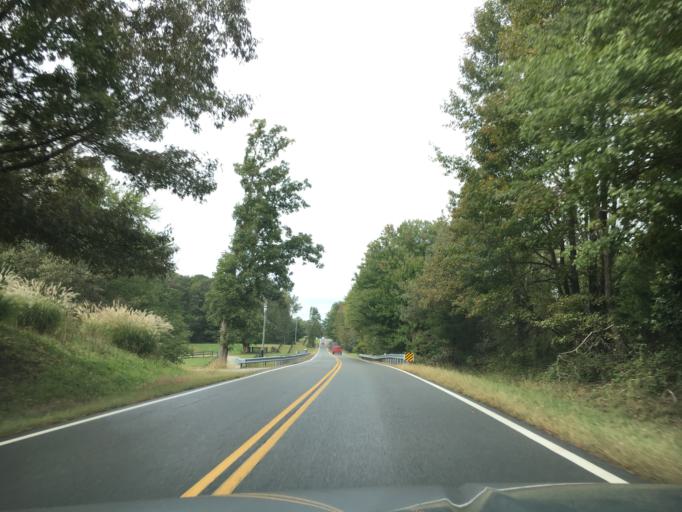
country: US
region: Virginia
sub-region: Goochland County
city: Goochland
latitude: 37.7416
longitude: -77.8464
